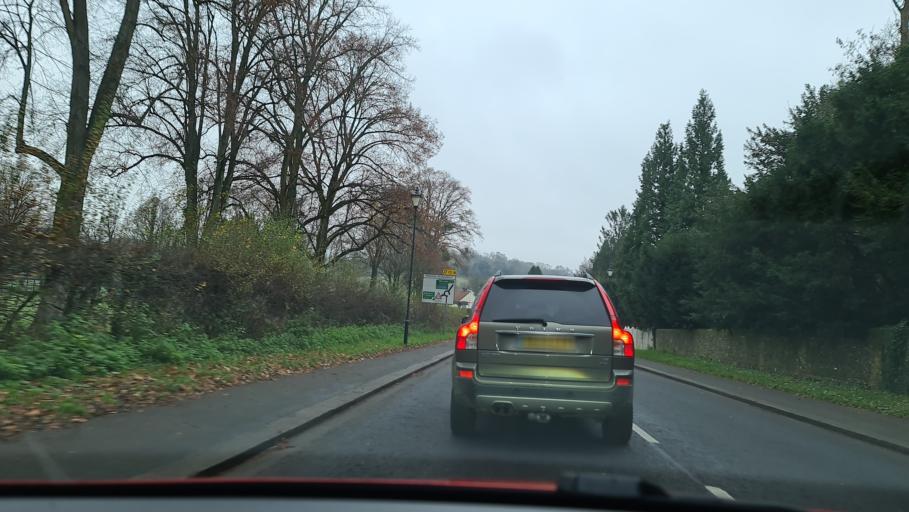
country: GB
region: England
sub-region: Buckinghamshire
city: High Wycombe
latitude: 51.6447
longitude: -0.7982
